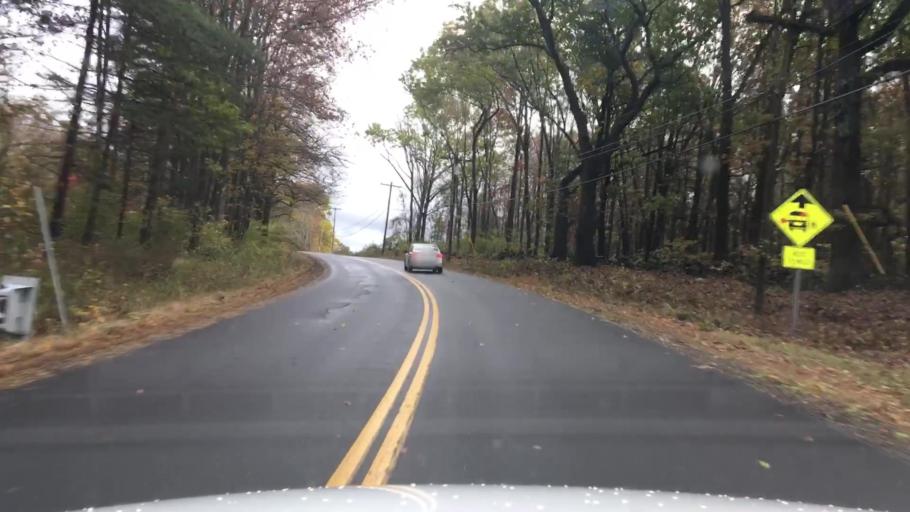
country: US
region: New Hampshire
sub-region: Strafford County
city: Lee
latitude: 43.0899
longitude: -70.9817
